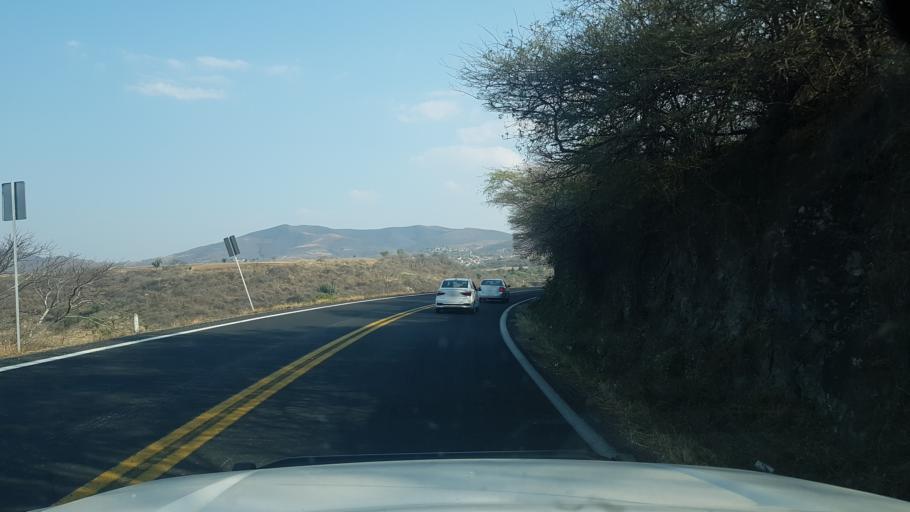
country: MX
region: Puebla
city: Calmeca
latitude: 18.6524
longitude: -98.6448
